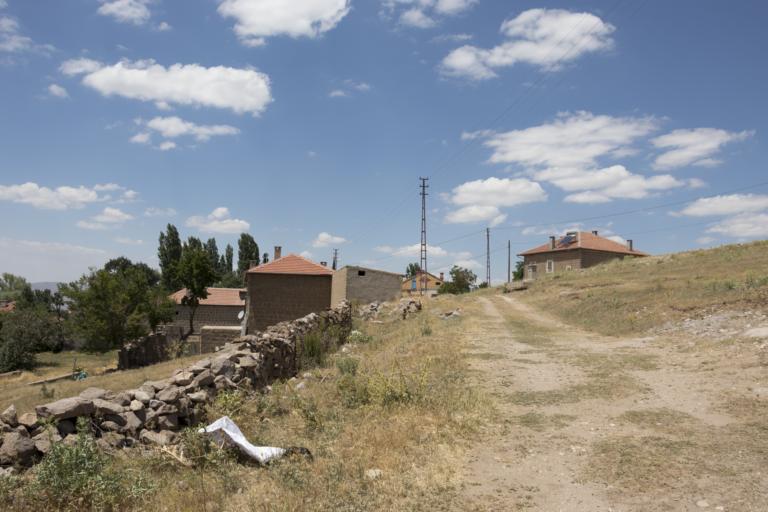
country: TR
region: Kayseri
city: Toklar
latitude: 38.4051
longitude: 36.0849
